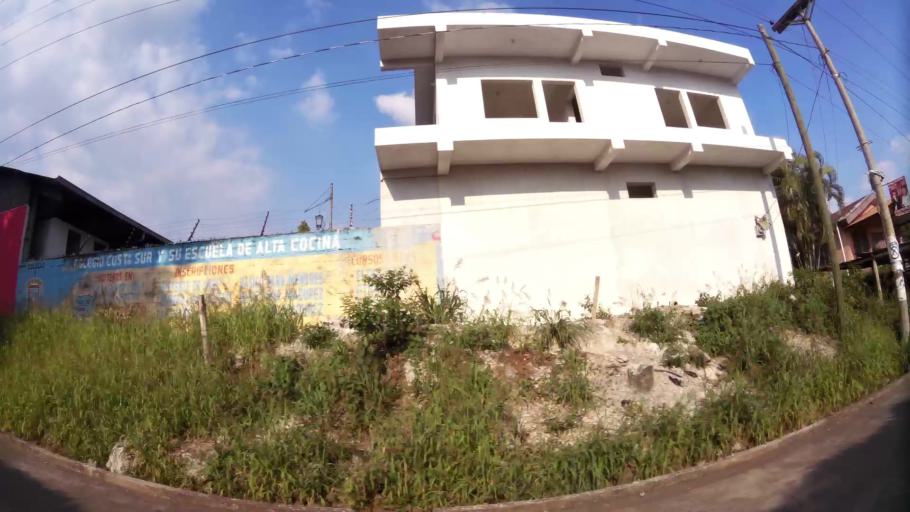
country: GT
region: Retalhuleu
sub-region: Municipio de Retalhuleu
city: Retalhuleu
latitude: 14.5333
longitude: -91.6736
